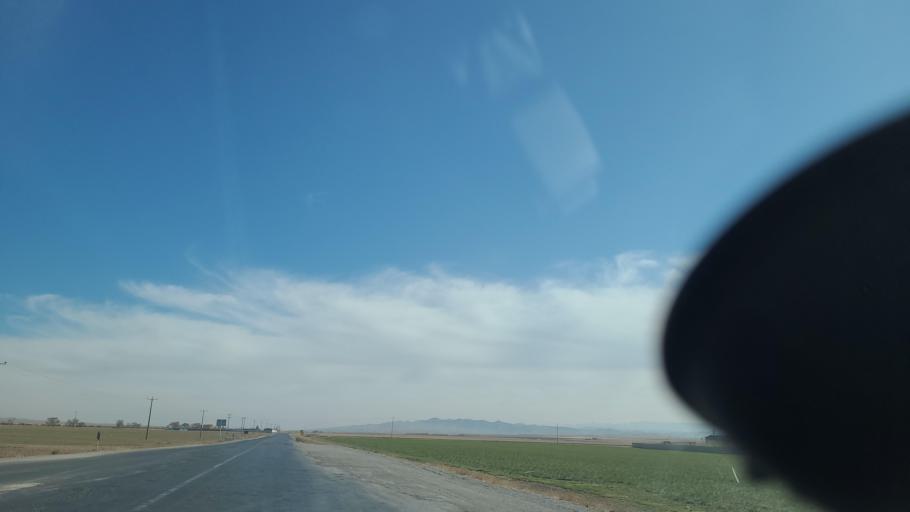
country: IR
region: Razavi Khorasan
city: Dowlatabad
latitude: 35.6002
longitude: 59.4602
